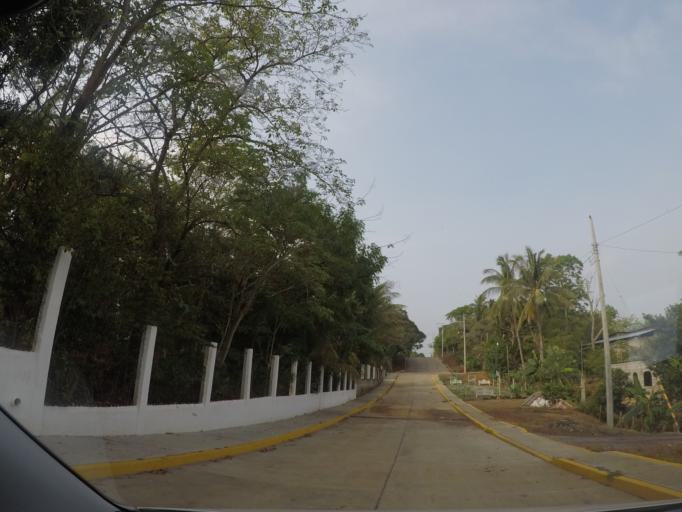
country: MX
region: Oaxaca
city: Colonia Rincon Viejo
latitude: 16.8871
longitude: -95.0471
